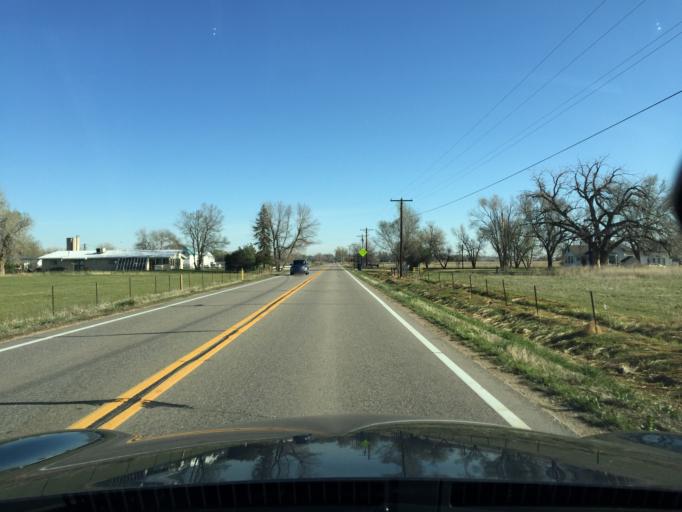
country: US
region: Colorado
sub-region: Boulder County
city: Erie
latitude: 40.0811
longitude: -105.0554
